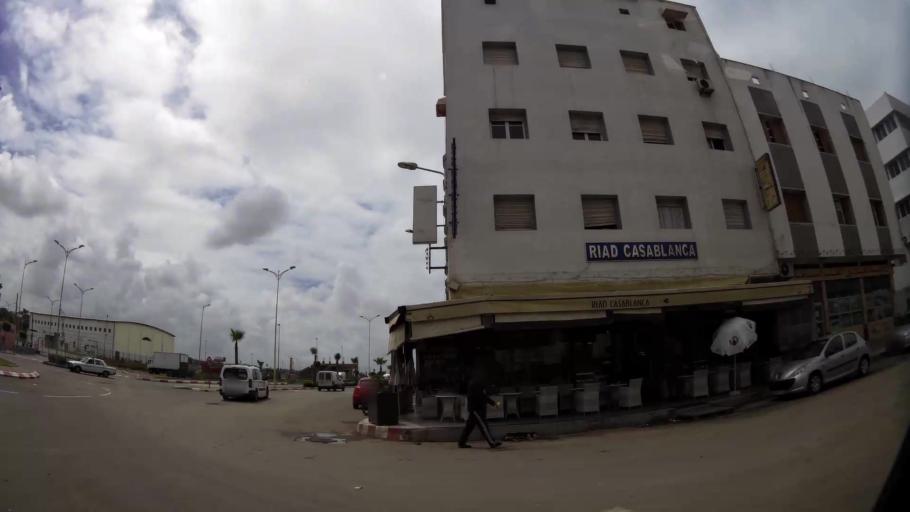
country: MA
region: Grand Casablanca
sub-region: Mediouna
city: Tit Mellil
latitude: 33.6052
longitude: -7.5046
